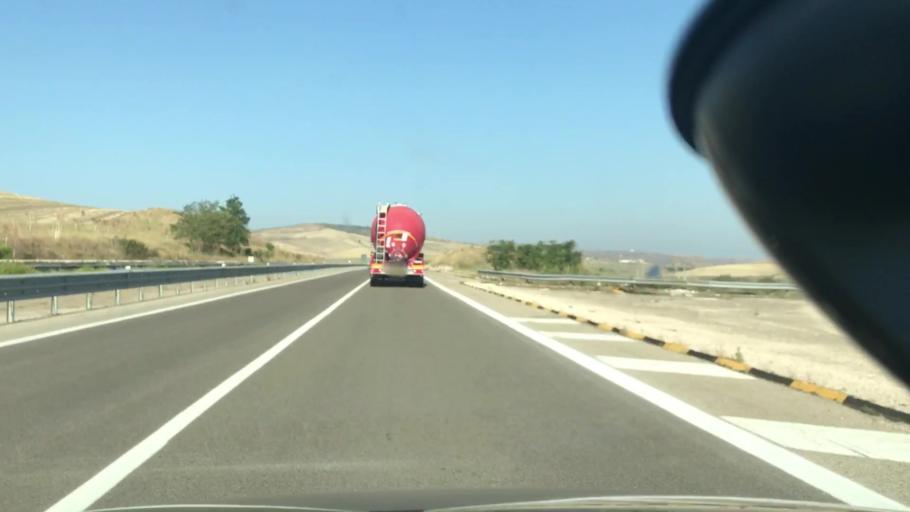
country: IT
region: Basilicate
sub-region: Provincia di Matera
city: Irsina
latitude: 40.7865
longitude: 16.2944
